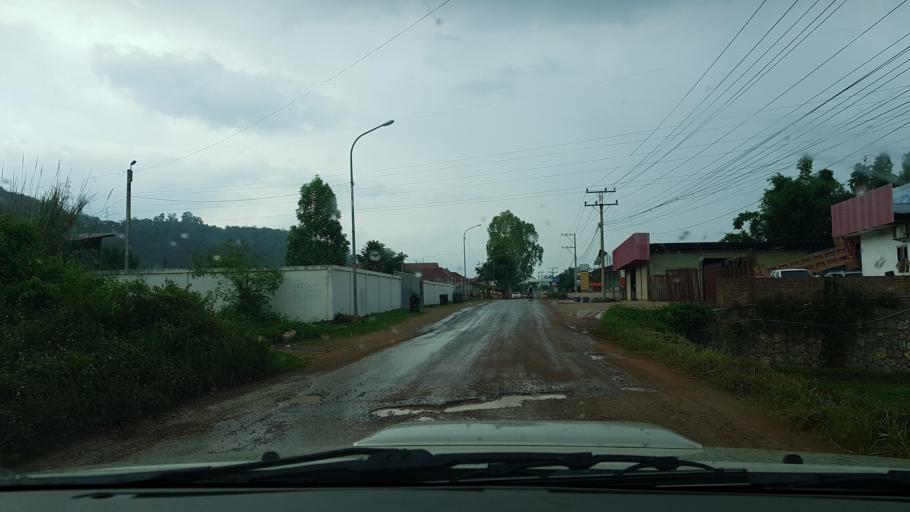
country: LA
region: Oudomxai
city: Muang Xay
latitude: 20.6411
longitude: 101.9726
